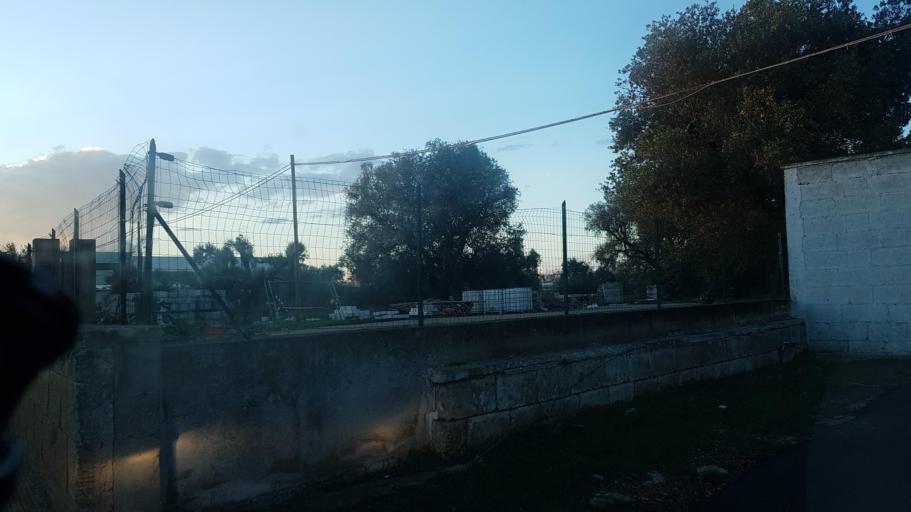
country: IT
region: Apulia
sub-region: Provincia di Brindisi
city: San Michele Salentino
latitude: 40.6305
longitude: 17.6391
